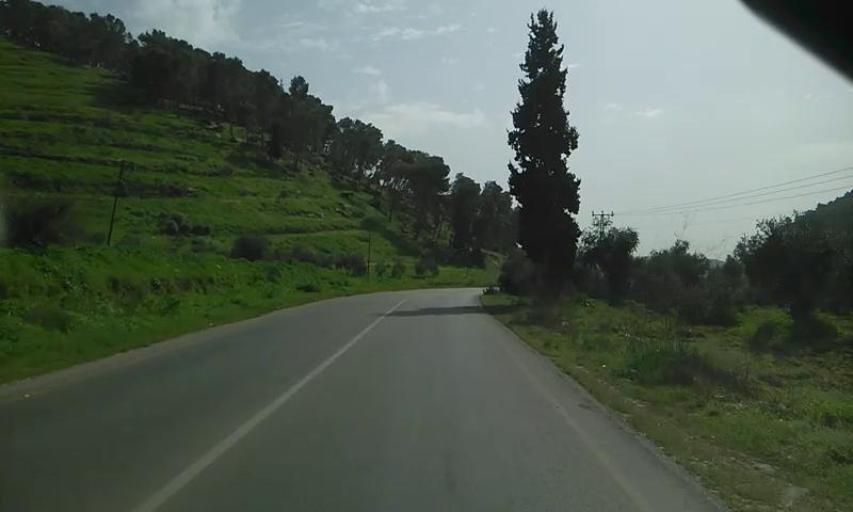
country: PS
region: West Bank
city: Mirkah
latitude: 32.4011
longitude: 35.2250
